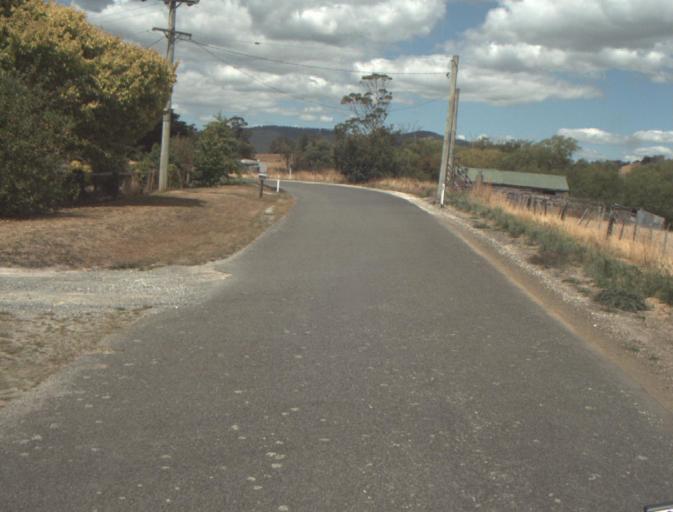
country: AU
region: Tasmania
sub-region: Launceston
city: Mayfield
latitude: -41.2239
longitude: 147.1374
